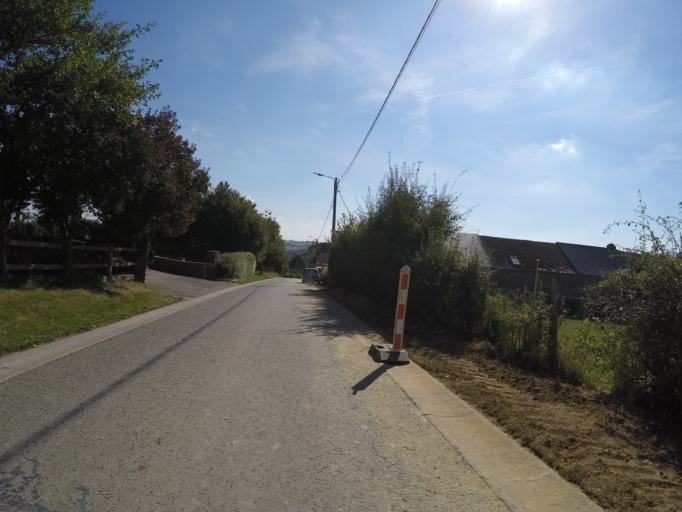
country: BE
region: Wallonia
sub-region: Province de Namur
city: Assesse
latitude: 50.3344
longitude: 5.0322
